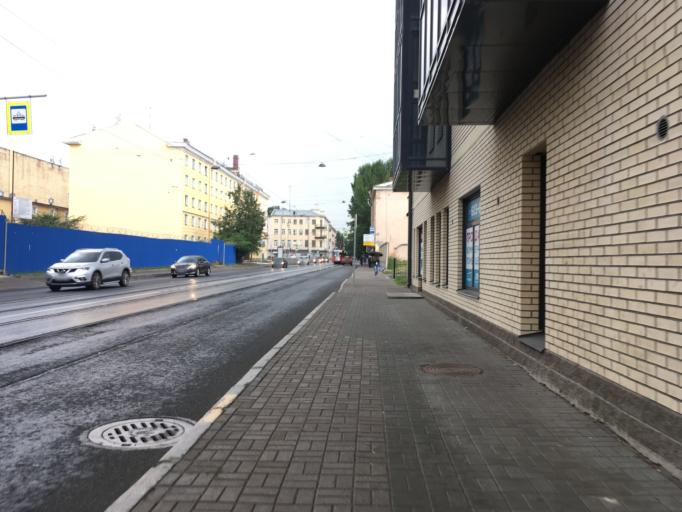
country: RU
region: St.-Petersburg
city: Centralniy
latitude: 59.9069
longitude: 30.3487
